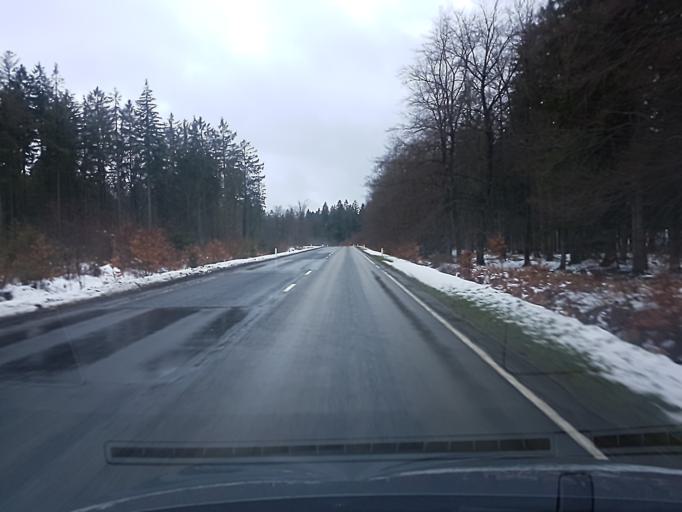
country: BE
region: Wallonia
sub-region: Province de Liege
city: Eupen
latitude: 50.5763
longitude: 6.0347
